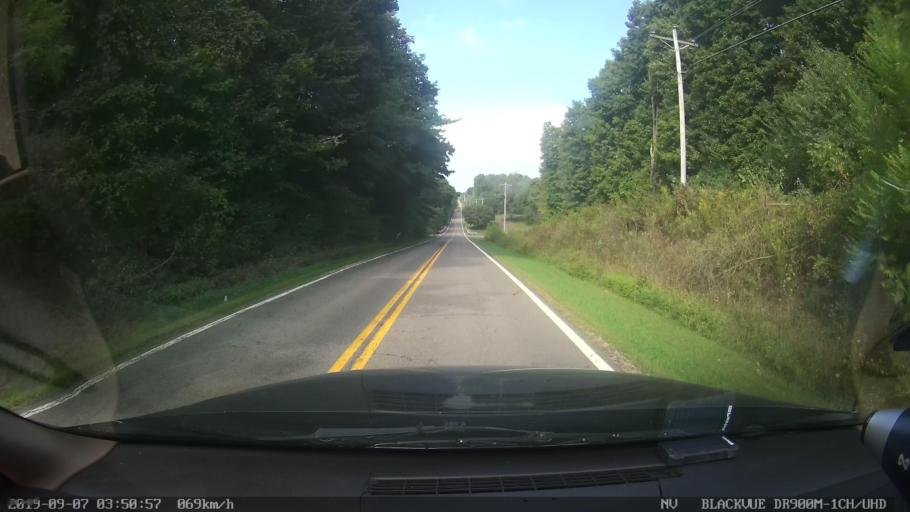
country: US
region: Ohio
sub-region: Licking County
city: Granville
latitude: 40.1535
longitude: -82.5464
